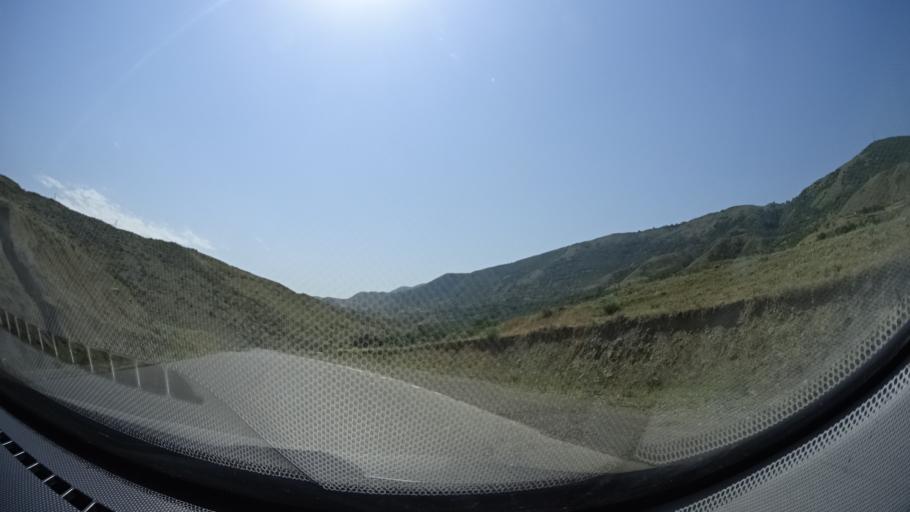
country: GE
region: Samtskhe-Javakheti
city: Aspindza
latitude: 41.6007
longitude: 43.1489
